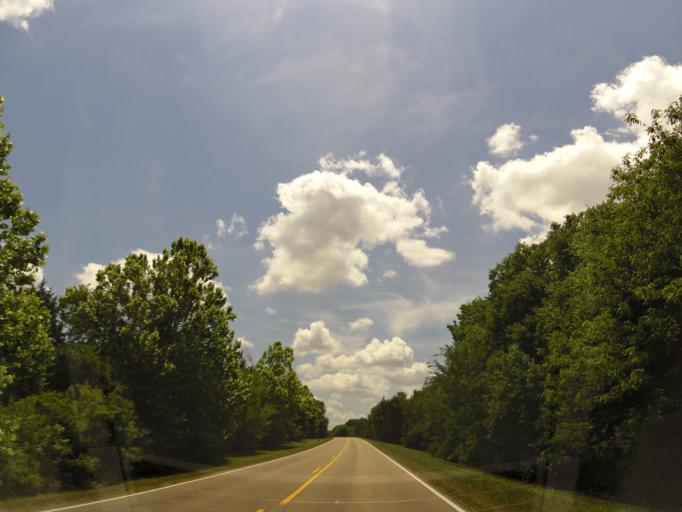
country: US
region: Mississippi
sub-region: Lee County
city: Tupelo
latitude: 34.2677
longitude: -88.7501
